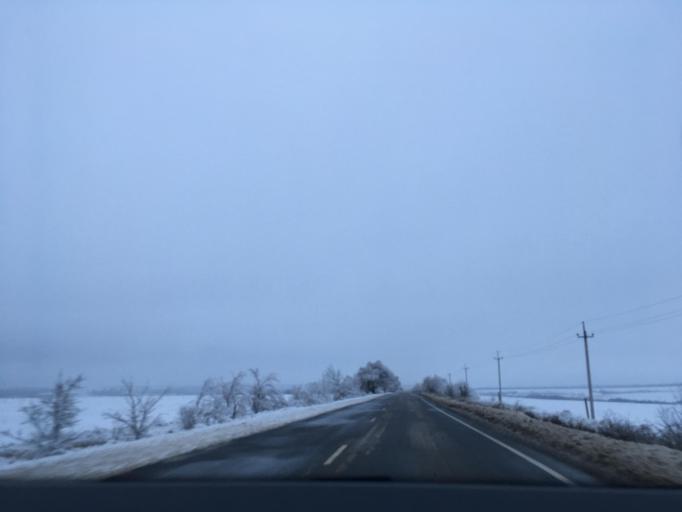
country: RU
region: Voronezj
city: Verkhniy Mamon
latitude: 50.0209
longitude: 40.1033
